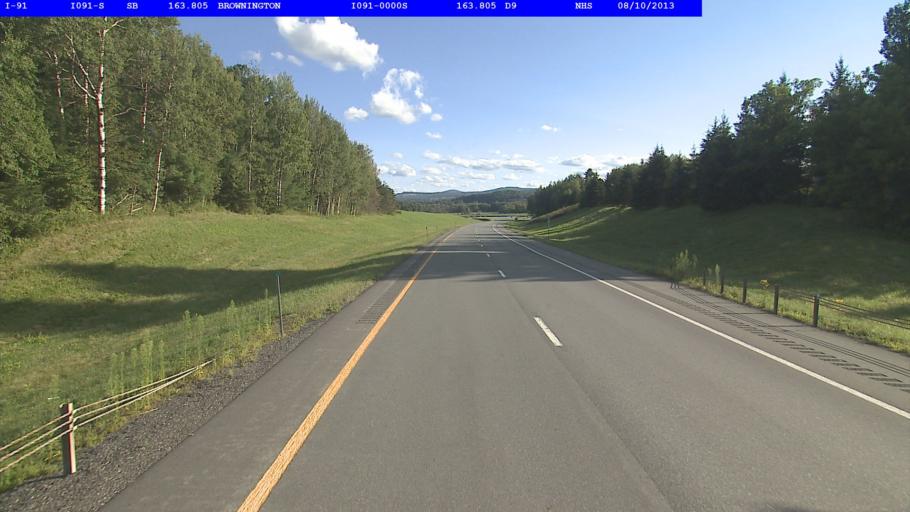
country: US
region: Vermont
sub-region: Orleans County
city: Newport
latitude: 44.8378
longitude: -72.1946
